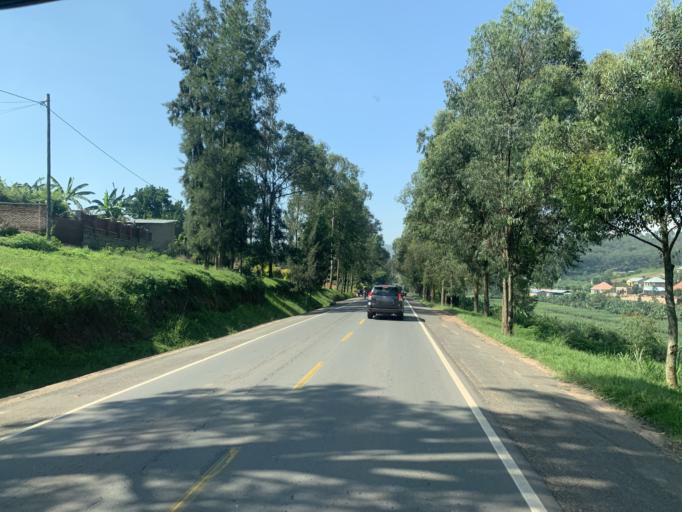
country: RW
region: Kigali
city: Kigali
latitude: -1.9872
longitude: 29.9326
